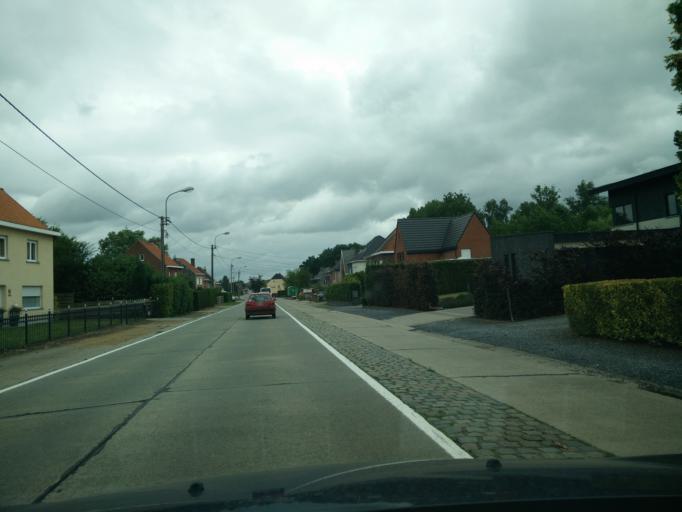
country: BE
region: Flanders
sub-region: Provincie Oost-Vlaanderen
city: Merelbeke
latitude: 50.9740
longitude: 3.7381
